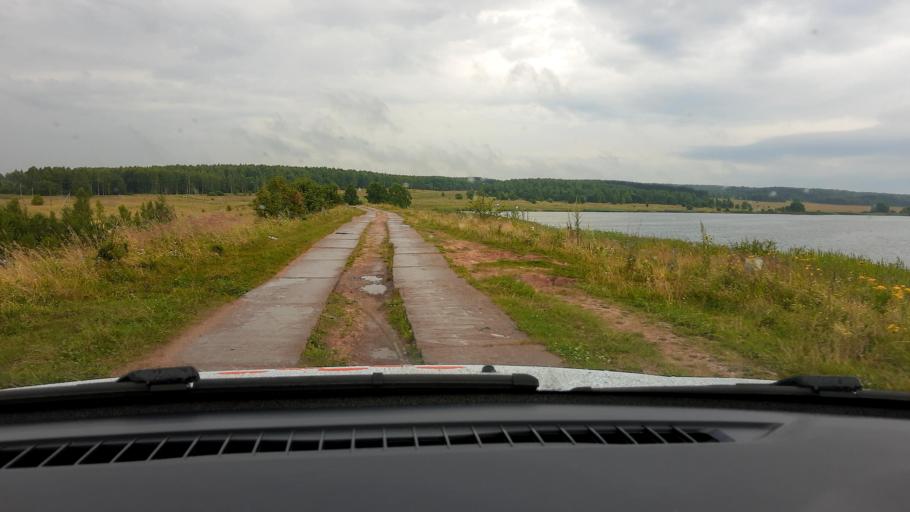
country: RU
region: Nizjnij Novgorod
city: Surovatikha
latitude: 55.9361
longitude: 43.9170
